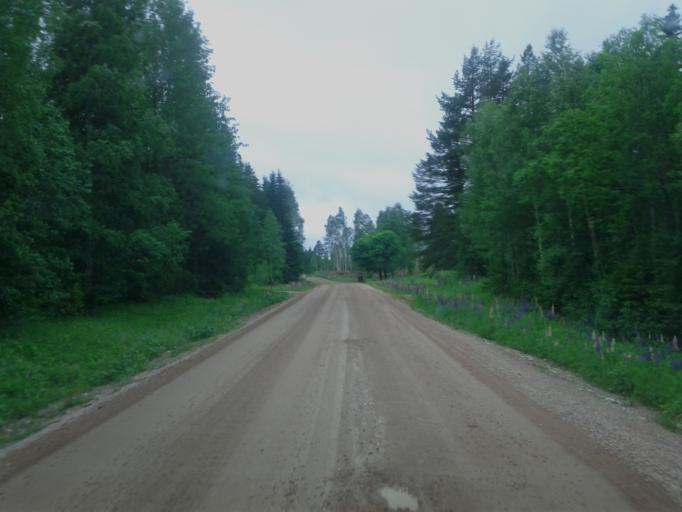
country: SE
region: Gaevleborg
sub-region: Hudiksvalls Kommun
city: Delsbo
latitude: 62.1416
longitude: 16.6170
